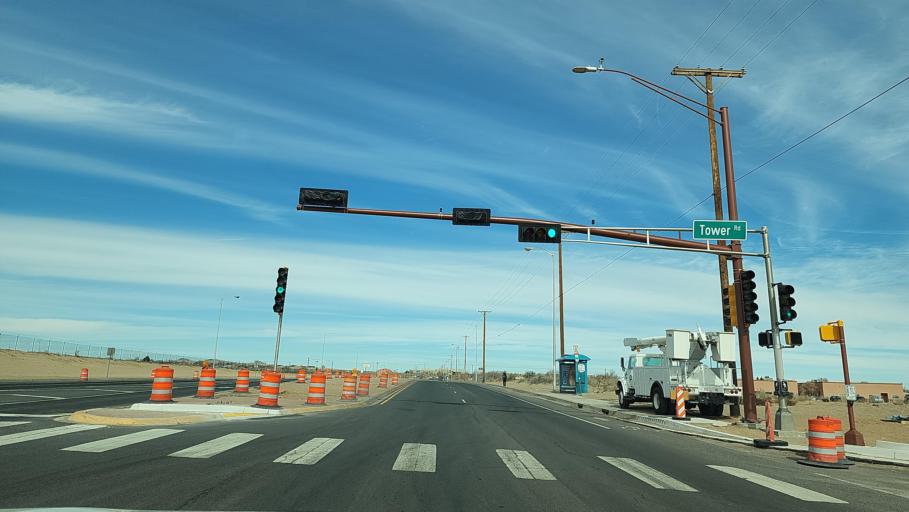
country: US
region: New Mexico
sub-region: Bernalillo County
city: Albuquerque
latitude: 35.0662
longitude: -106.7102
